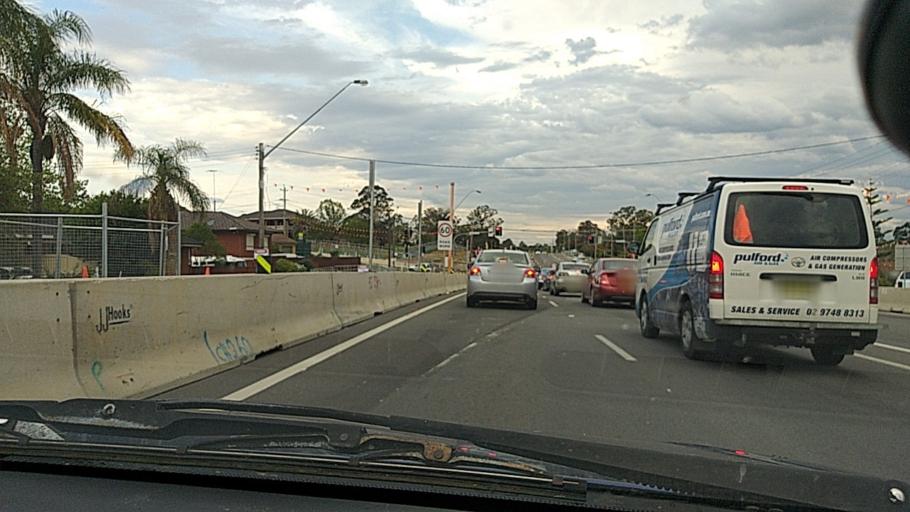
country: AU
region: New South Wales
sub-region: Penrith Municipality
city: Kingswood Park
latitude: -33.7670
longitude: 150.7100
